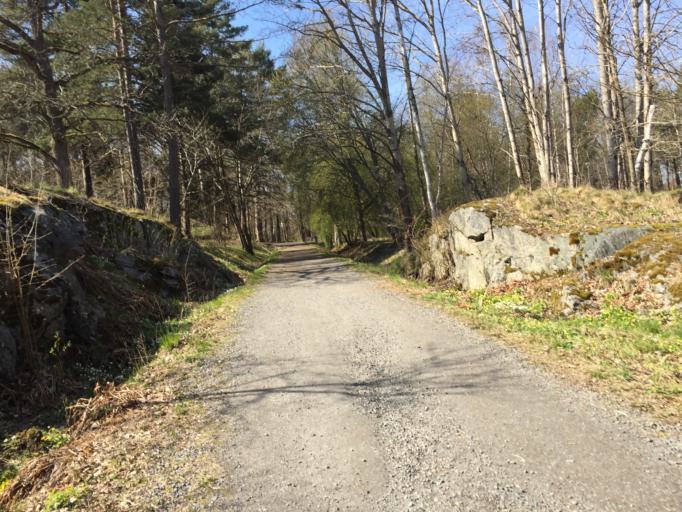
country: SE
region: Stockholm
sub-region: Nacka Kommun
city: Alta
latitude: 59.2700
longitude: 18.1467
